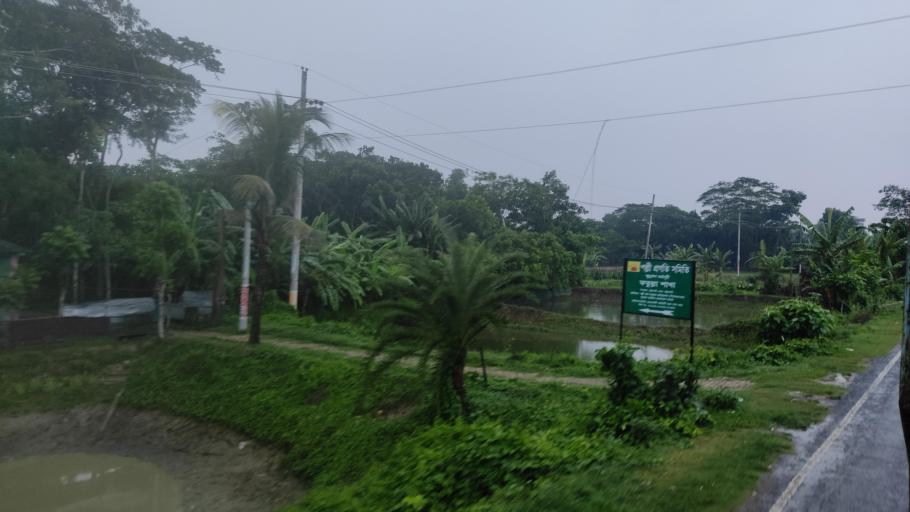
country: BD
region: Barisal
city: Bhandaria
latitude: 22.2915
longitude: 90.3254
